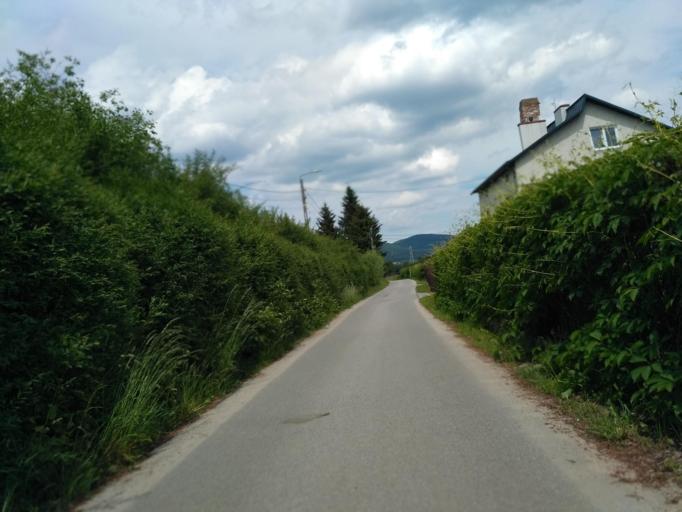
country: PL
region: Subcarpathian Voivodeship
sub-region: Powiat krosnienski
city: Odrzykon
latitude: 49.7162
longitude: 21.7442
